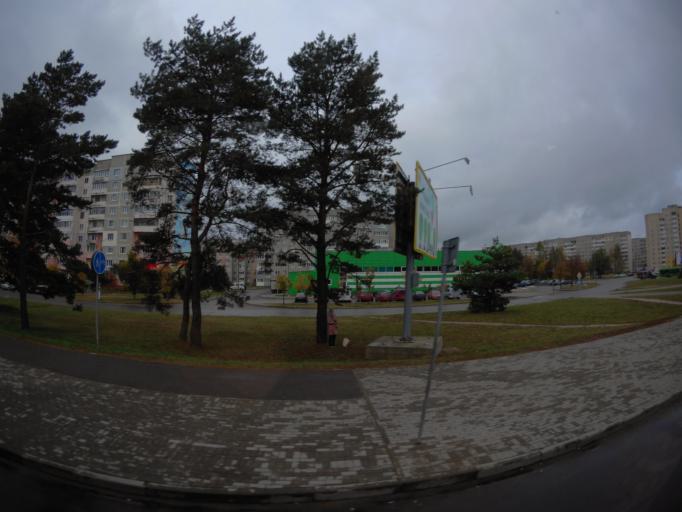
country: BY
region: Minsk
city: Horad Barysaw
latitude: 54.2025
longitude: 28.4809
